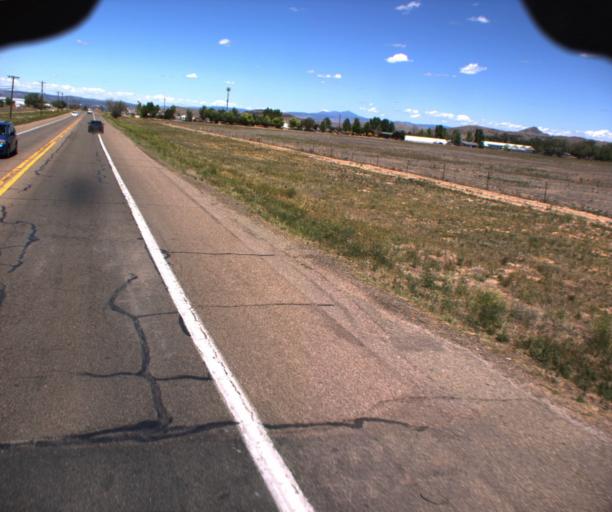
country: US
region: Arizona
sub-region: Yavapai County
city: Chino Valley
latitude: 34.7789
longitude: -112.4526
